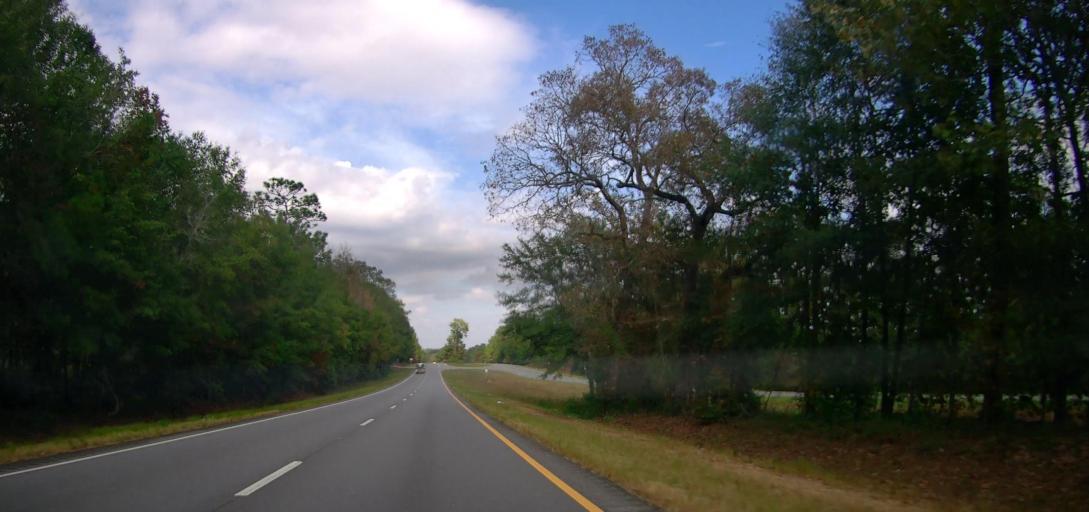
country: US
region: Georgia
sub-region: Grady County
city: Cairo
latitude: 30.7354
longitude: -84.1141
